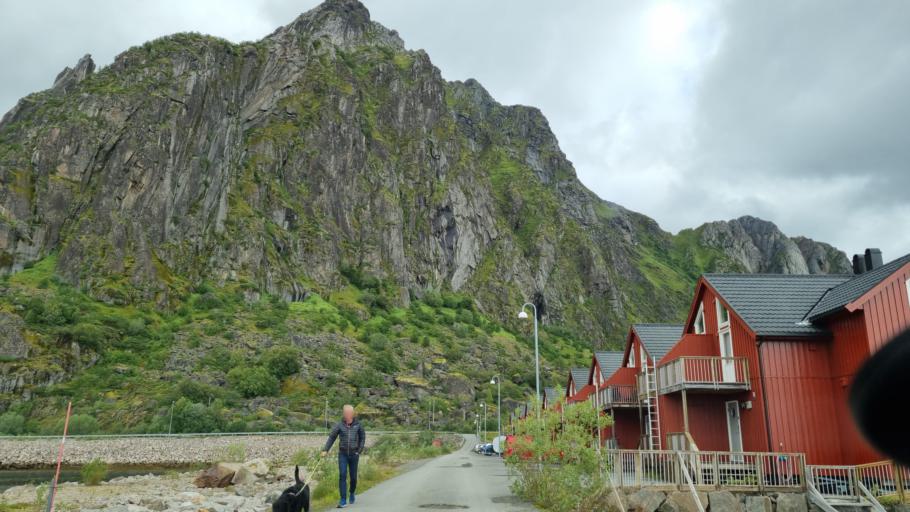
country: NO
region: Nordland
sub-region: Vagan
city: Svolvaer
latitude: 68.2403
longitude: 14.5900
